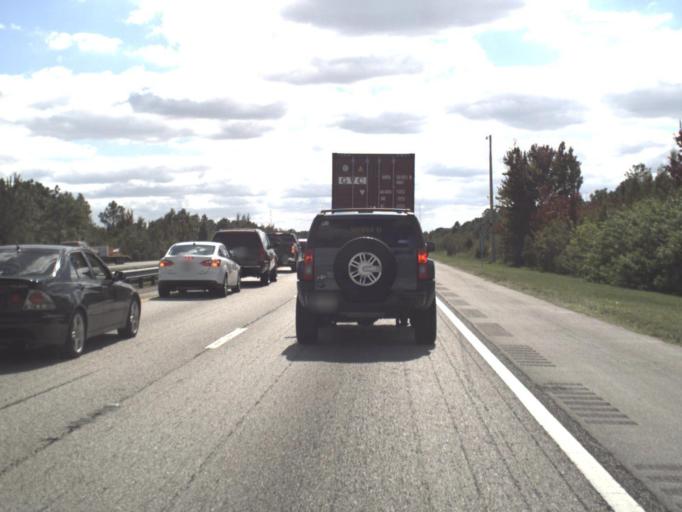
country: US
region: Florida
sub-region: Orange County
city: Southchase
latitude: 28.3989
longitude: -81.3915
